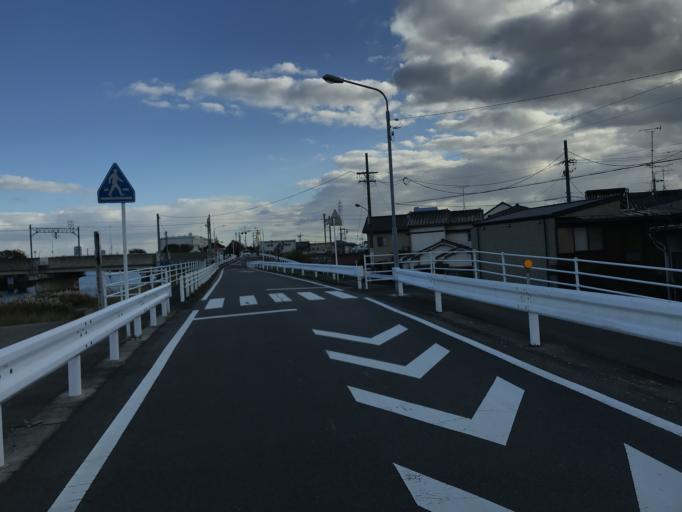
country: JP
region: Aichi
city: Nagoya-shi
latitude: 35.1978
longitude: 136.8366
